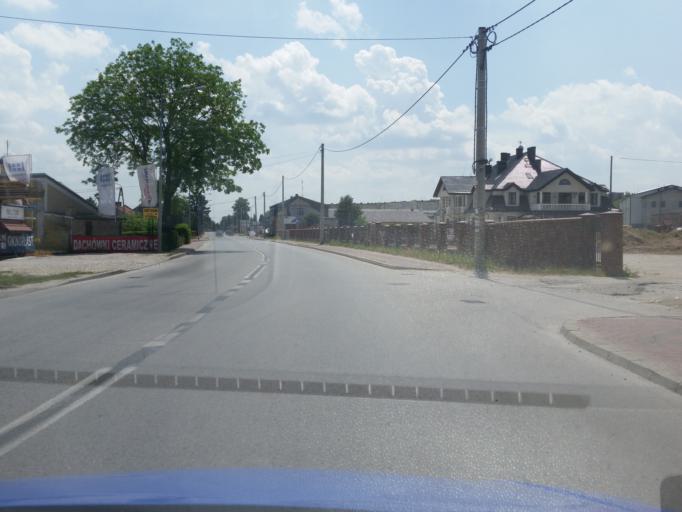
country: PL
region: Swietokrzyskie
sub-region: Powiat kazimierski
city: Kazimierza Wielka
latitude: 50.2758
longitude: 20.4809
